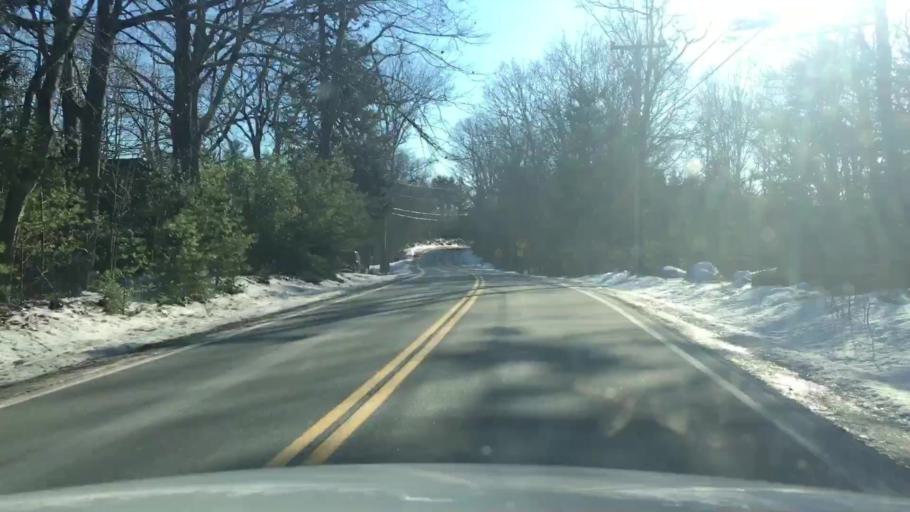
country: US
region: Maine
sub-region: Hancock County
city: Orland
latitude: 44.5138
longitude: -68.7527
